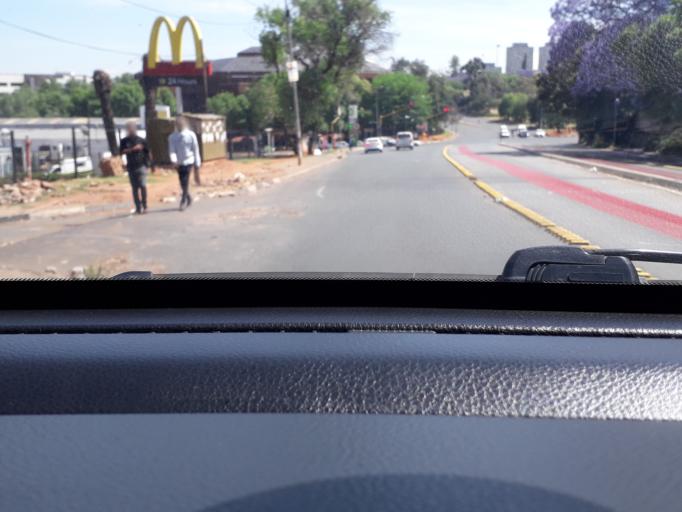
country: ZA
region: Gauteng
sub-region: City of Johannesburg Metropolitan Municipality
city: Johannesburg
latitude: -26.1864
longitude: 28.0409
